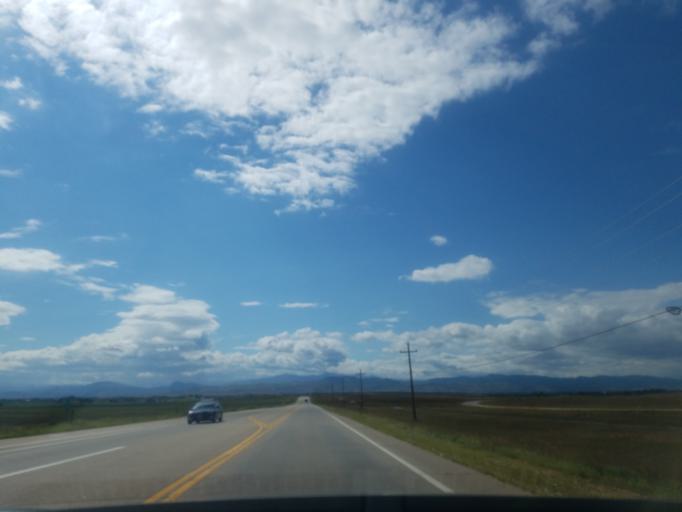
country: US
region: Colorado
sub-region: Larimer County
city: Loveland
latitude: 40.4797
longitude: -105.0089
